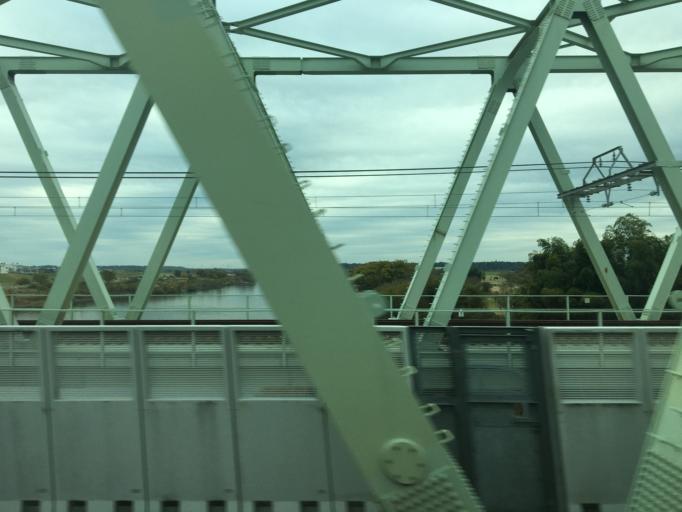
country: JP
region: Ibaraki
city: Toride
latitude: 35.8891
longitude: 140.0585
